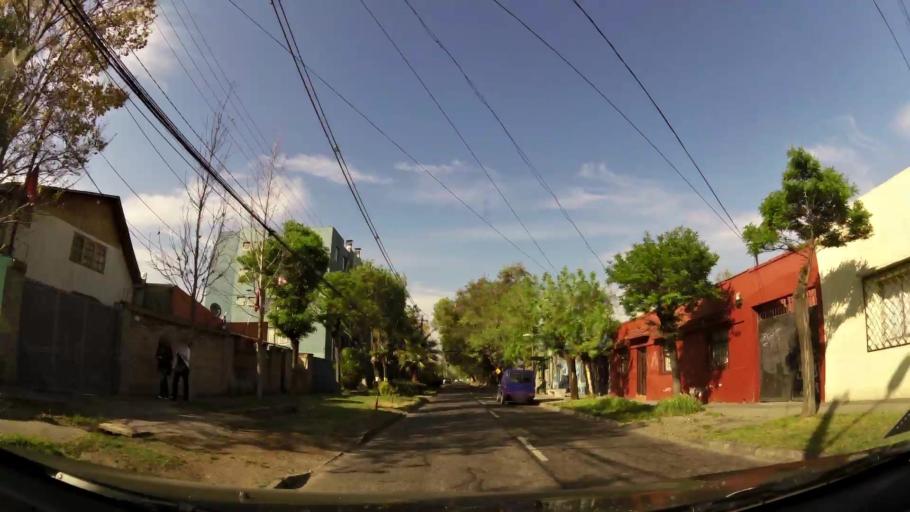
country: CL
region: Santiago Metropolitan
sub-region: Provincia de Maipo
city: San Bernardo
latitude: -33.5995
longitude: -70.7020
